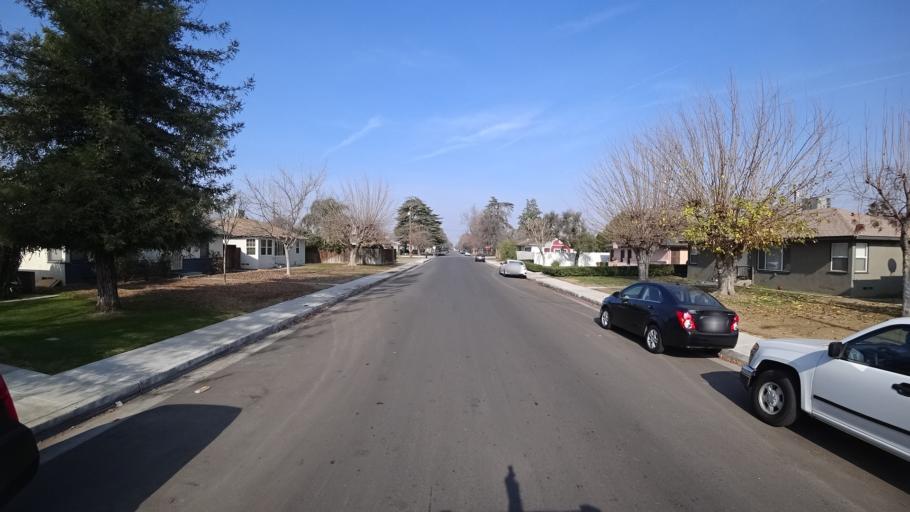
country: US
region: California
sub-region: Kern County
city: Bakersfield
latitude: 35.3572
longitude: -119.0362
